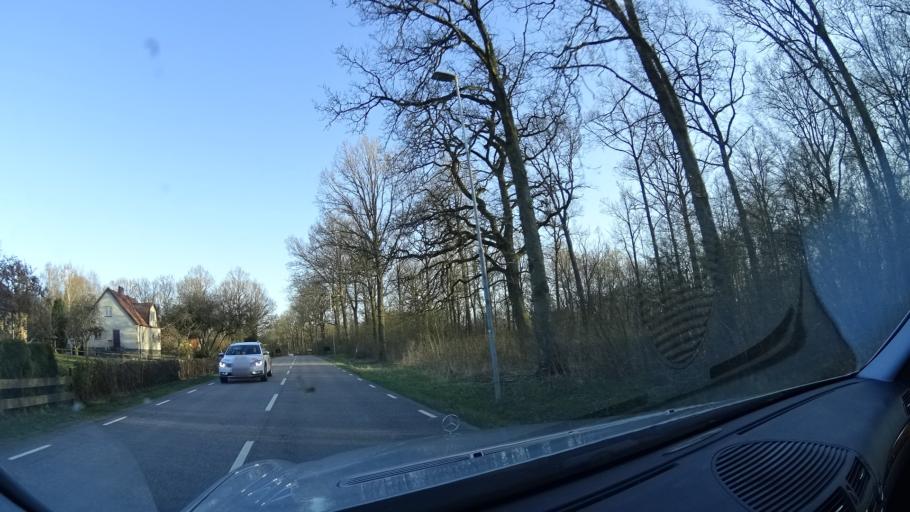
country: SE
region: Skane
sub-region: Svalovs Kommun
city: Kagerod
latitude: 55.9955
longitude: 13.0966
